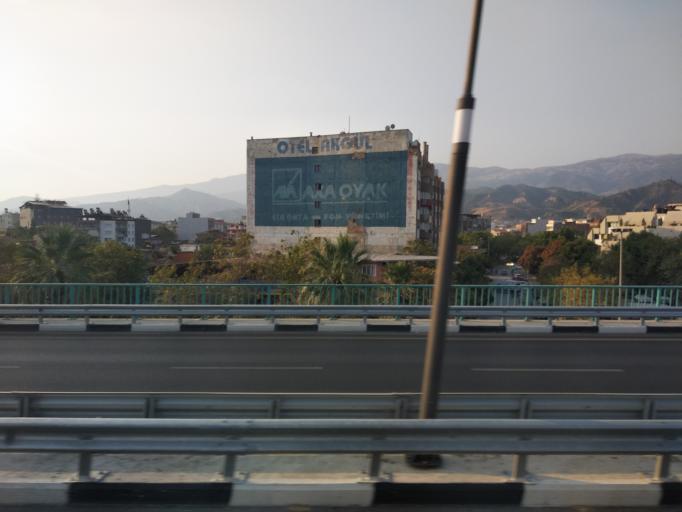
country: TR
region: Manisa
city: Salihli
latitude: 38.4899
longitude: 28.1379
